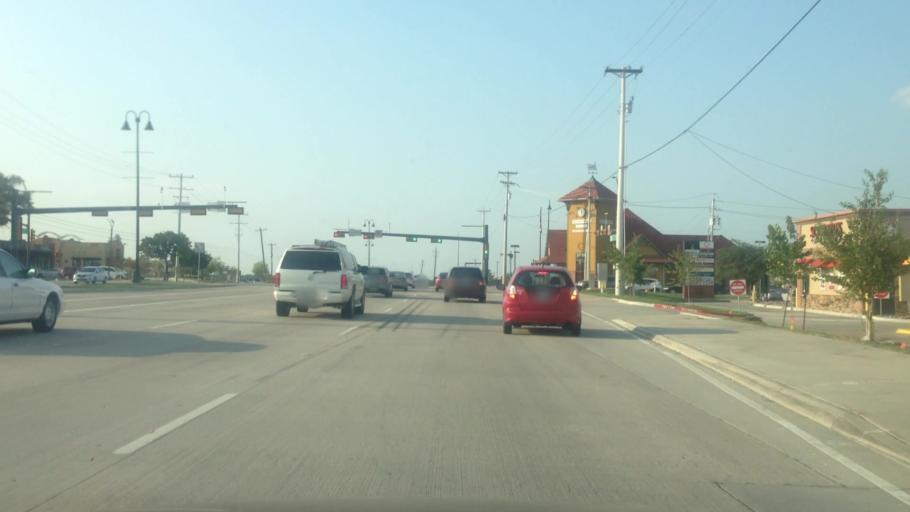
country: US
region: Texas
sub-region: Denton County
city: The Colony
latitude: 33.0797
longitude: -96.8926
